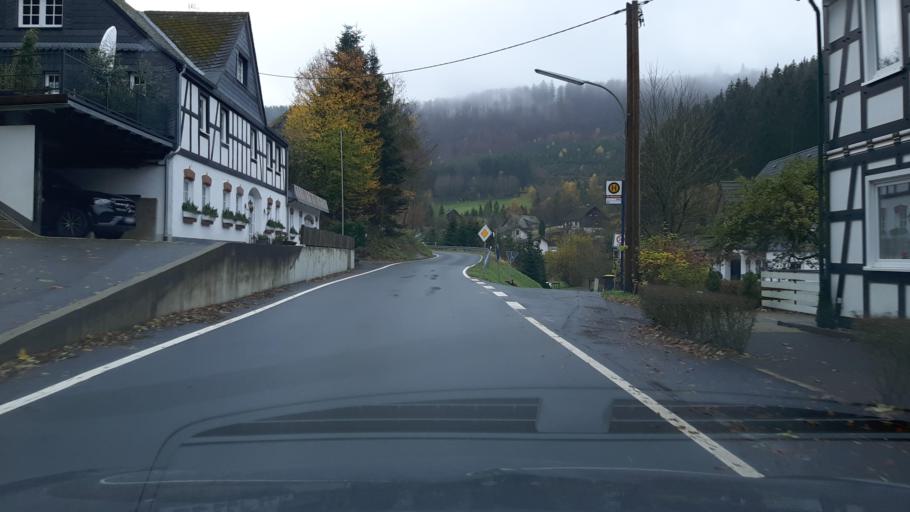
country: DE
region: North Rhine-Westphalia
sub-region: Regierungsbezirk Arnsberg
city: Bad Fredeburg
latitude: 51.1977
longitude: 8.4059
